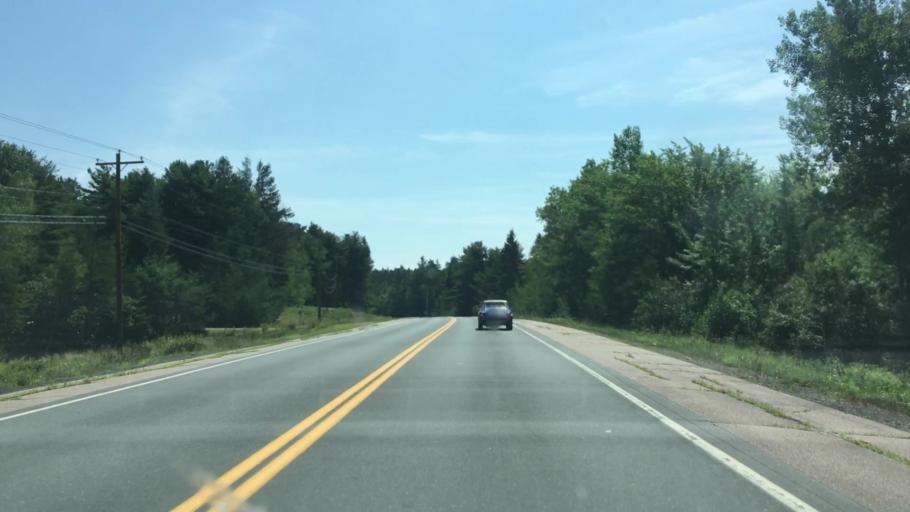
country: US
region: Maine
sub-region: Washington County
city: Calais
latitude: 45.1593
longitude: -67.1897
